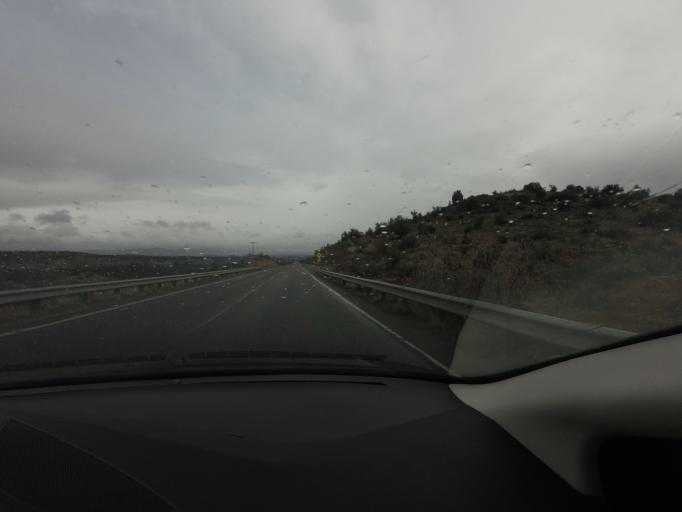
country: US
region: Arizona
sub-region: Yavapai County
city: Lake Montezuma
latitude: 34.6690
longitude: -111.8315
